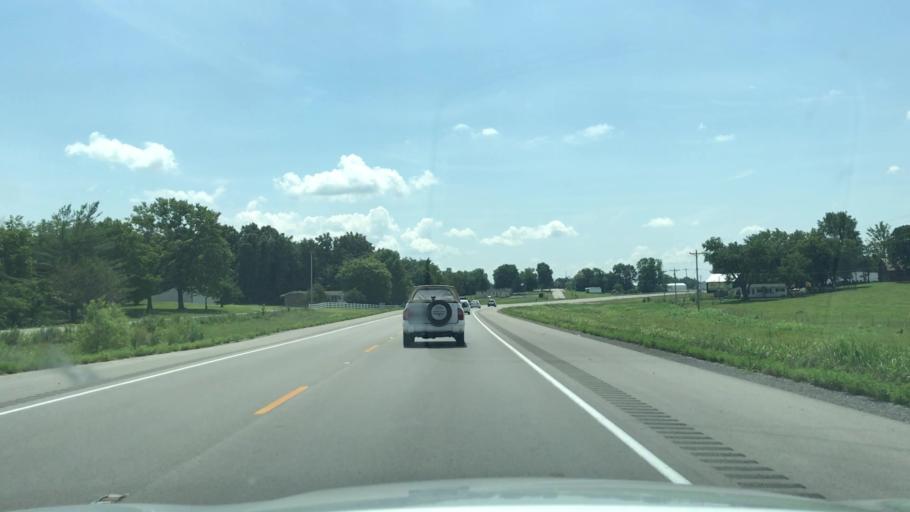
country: US
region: Tennessee
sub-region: Pickett County
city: Byrdstown
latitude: 36.6278
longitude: -85.0912
